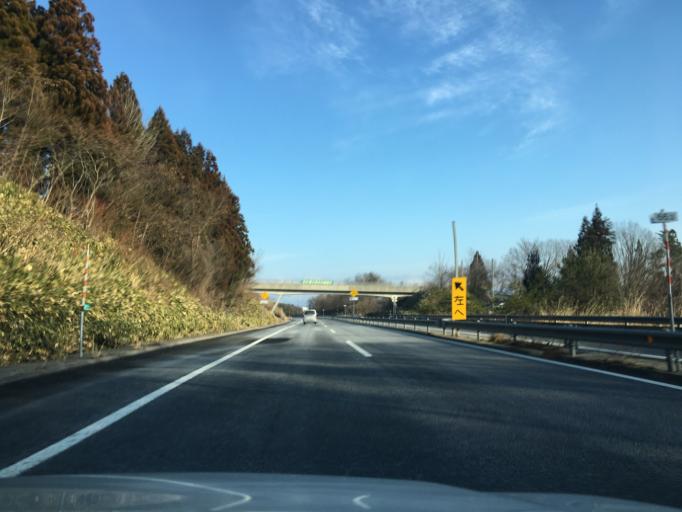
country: JP
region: Yamagata
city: Sagae
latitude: 38.4225
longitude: 140.1713
